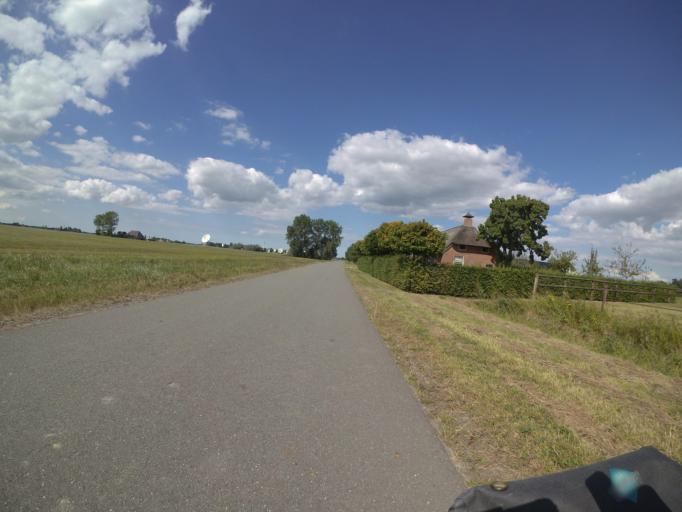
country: NL
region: Friesland
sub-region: Gemeente Kollumerland en Nieuwkruisland
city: Kollum
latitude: 53.2755
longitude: 6.2242
